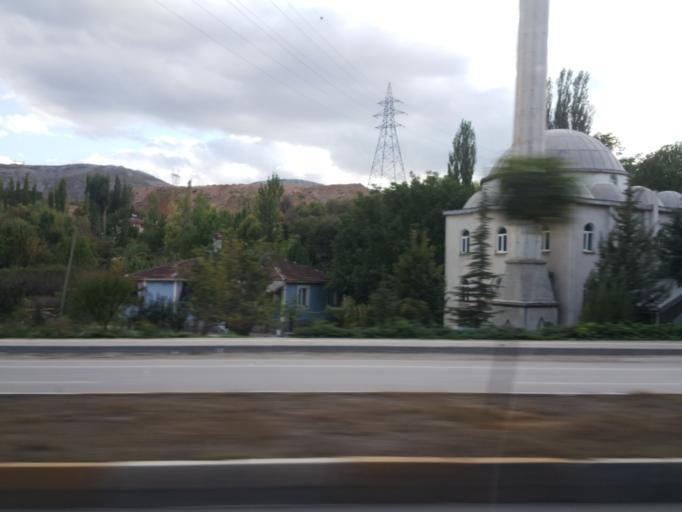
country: TR
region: Tokat
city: Tokat
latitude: 40.3379
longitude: 36.4993
